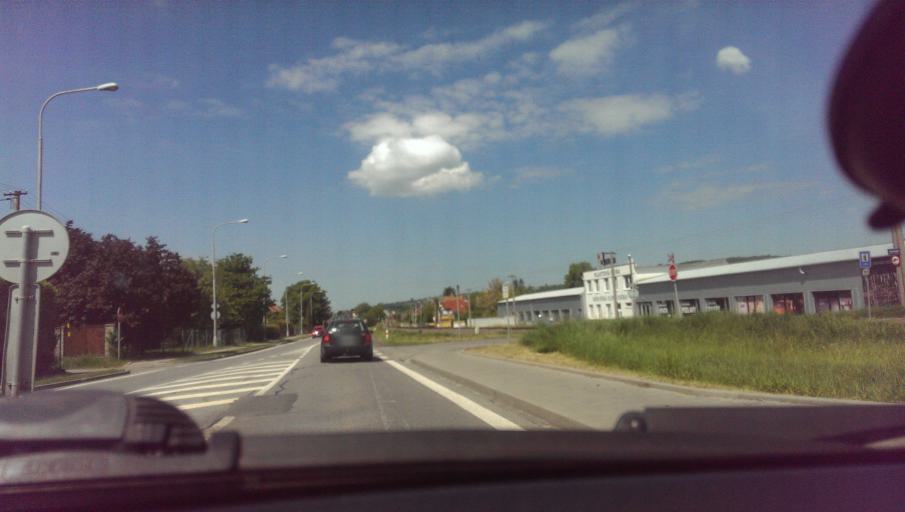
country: CZ
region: Zlin
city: Hvozdna
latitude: 49.2172
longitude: 17.7536
